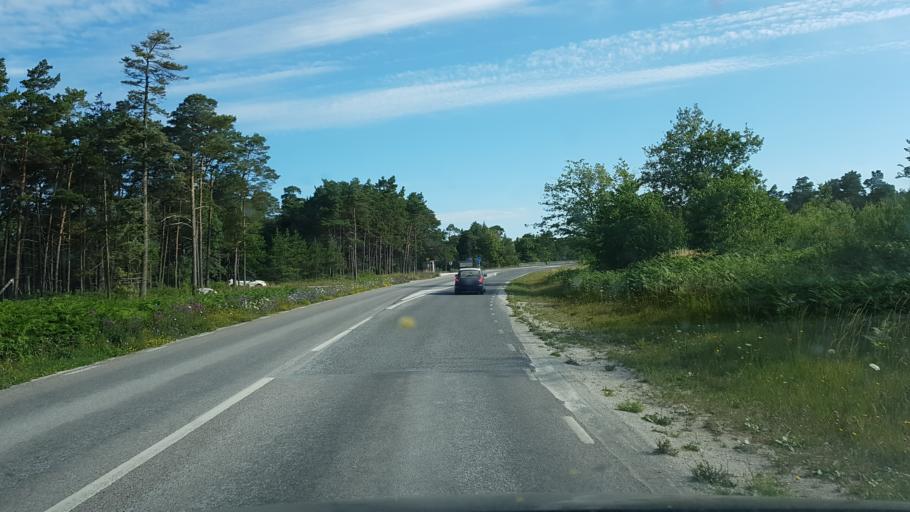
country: SE
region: Gotland
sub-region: Gotland
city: Visby
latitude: 57.7336
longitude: 18.4056
